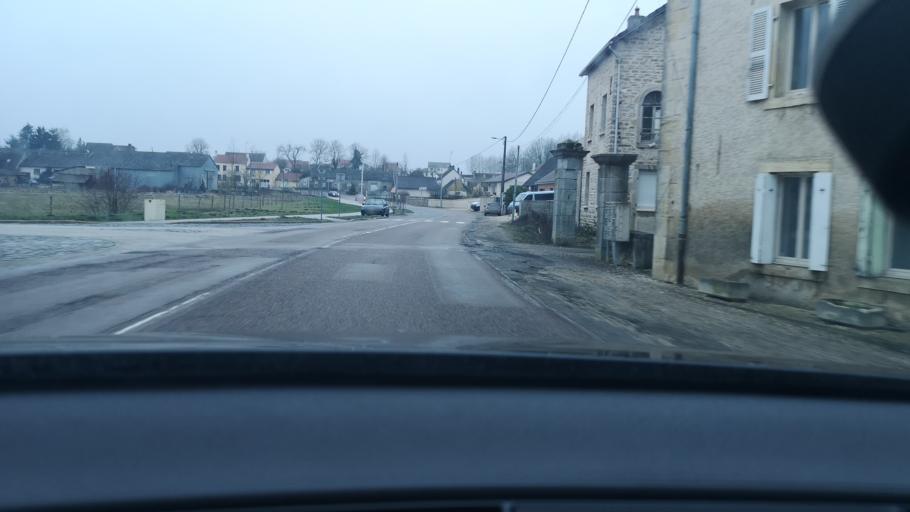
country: FR
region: Bourgogne
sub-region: Departement de la Cote-d'Or
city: Fenay
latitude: 47.2251
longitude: 5.0628
